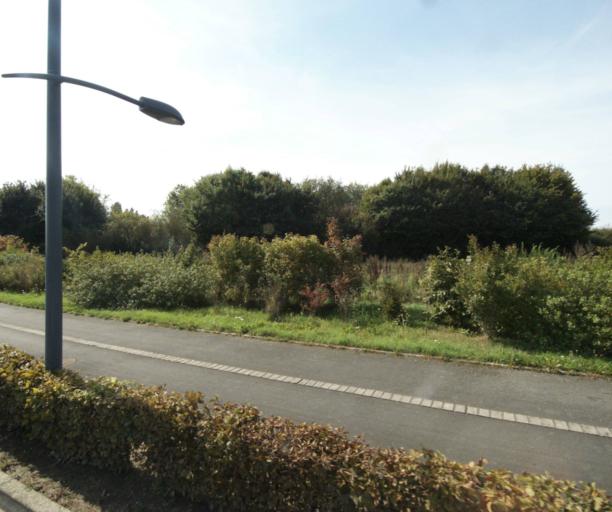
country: FR
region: Nord-Pas-de-Calais
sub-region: Departement du Nord
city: Hallennes-lez-Haubourdin
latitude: 50.6237
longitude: 2.9616
